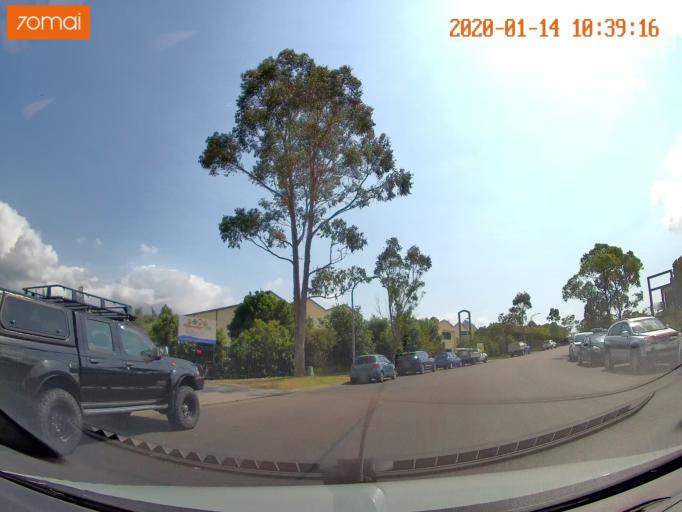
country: AU
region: New South Wales
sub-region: Lake Macquarie Shire
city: Dora Creek
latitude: -33.1150
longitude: 151.4762
